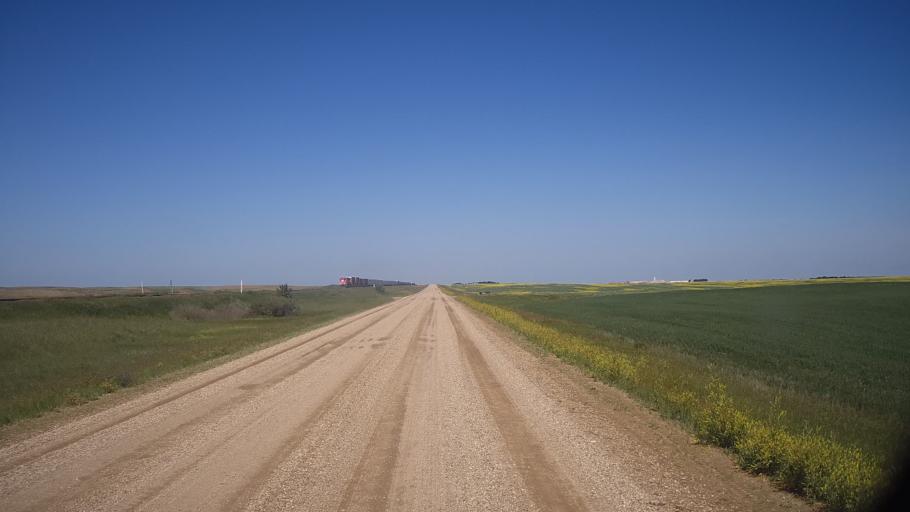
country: CA
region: Saskatchewan
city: Watrous
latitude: 51.8546
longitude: -105.9461
